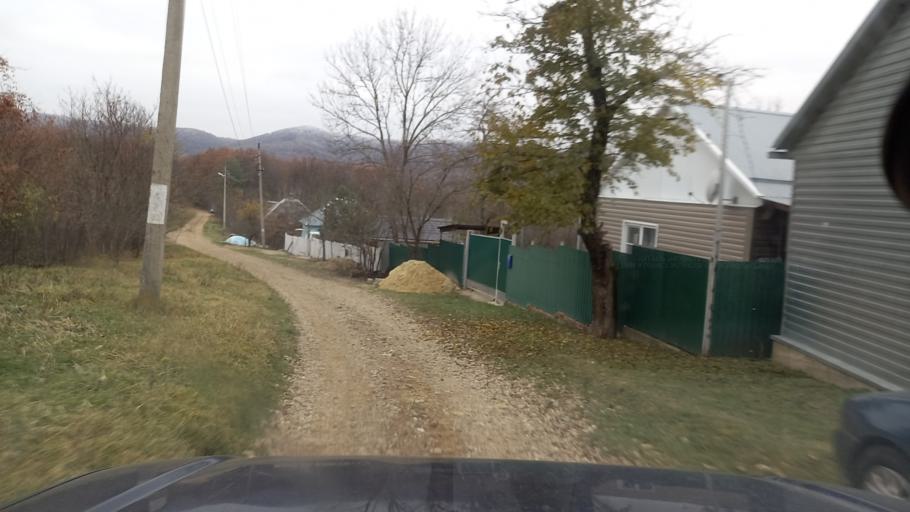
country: RU
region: Krasnodarskiy
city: Goryachiy Klyuch
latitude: 44.5131
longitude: 39.2952
